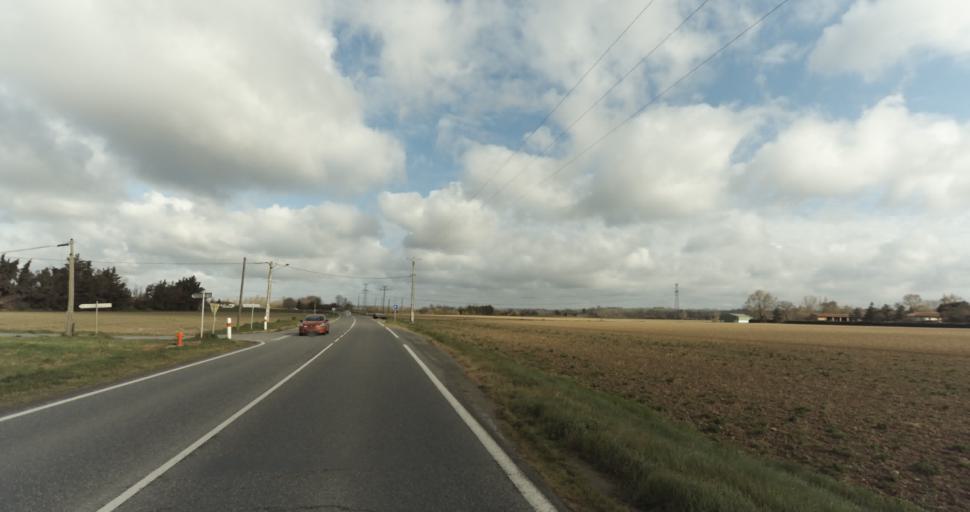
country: FR
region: Midi-Pyrenees
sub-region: Departement de la Haute-Garonne
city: Miremont
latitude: 43.3795
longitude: 1.4451
